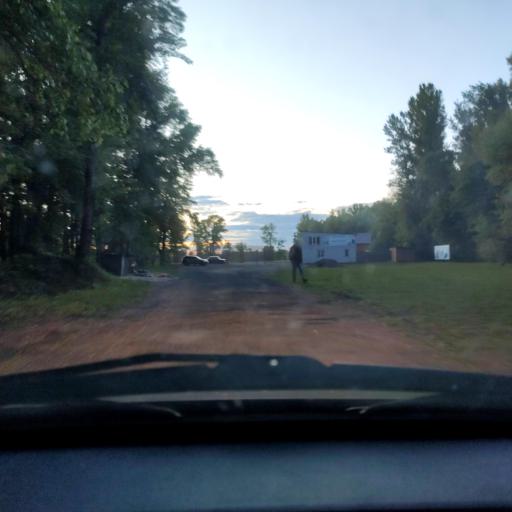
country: RU
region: Bashkortostan
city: Ufa
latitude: 54.8140
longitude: 56.0445
